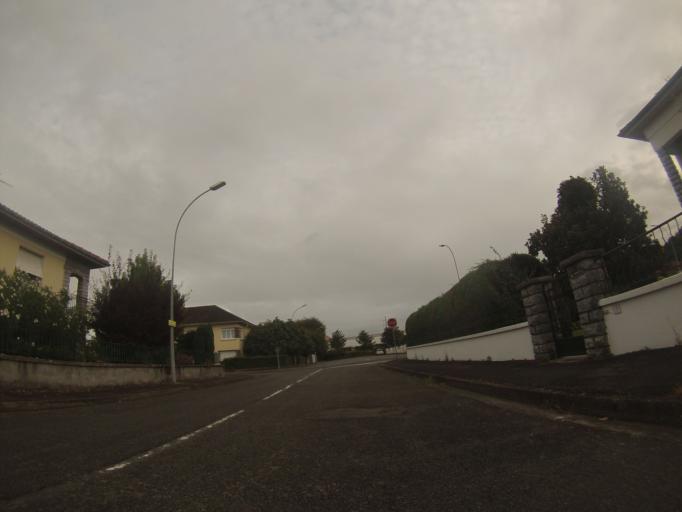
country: FR
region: Aquitaine
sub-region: Departement des Pyrenees-Atlantiques
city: Gelos
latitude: 43.2812
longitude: -0.3634
